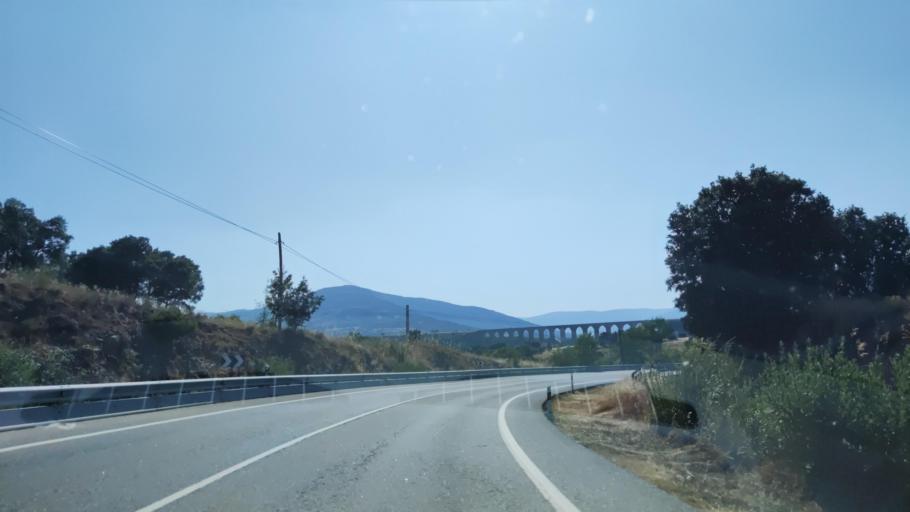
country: ES
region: Madrid
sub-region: Provincia de Madrid
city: Garganta de los Montes
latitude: 40.9428
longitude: -3.7150
